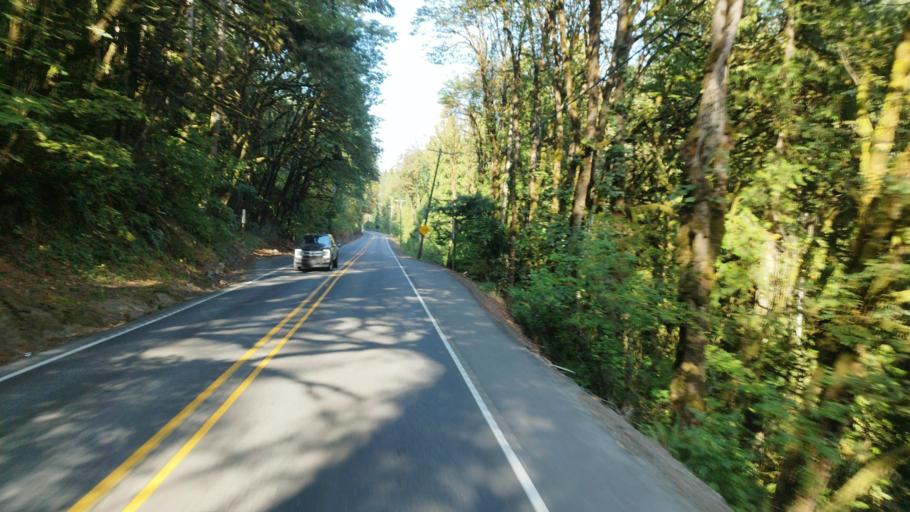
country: US
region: Oregon
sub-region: Washington County
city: Bethany
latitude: 45.6394
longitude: -122.8610
